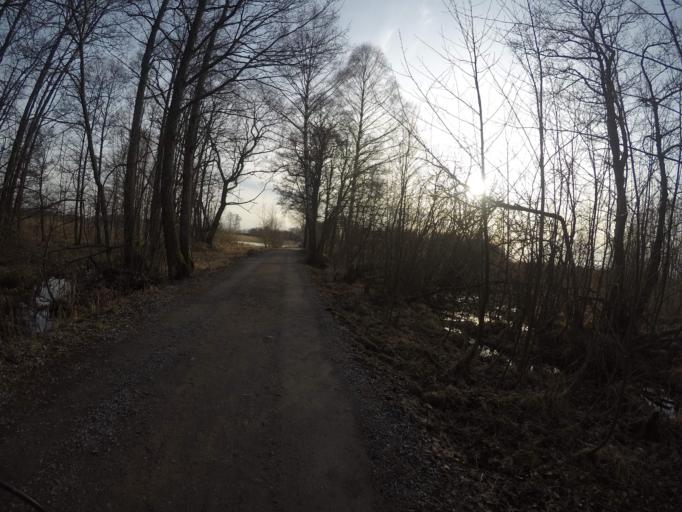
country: SE
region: Soedermanland
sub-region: Eskilstuna Kommun
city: Kvicksund
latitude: 59.4574
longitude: 16.3073
